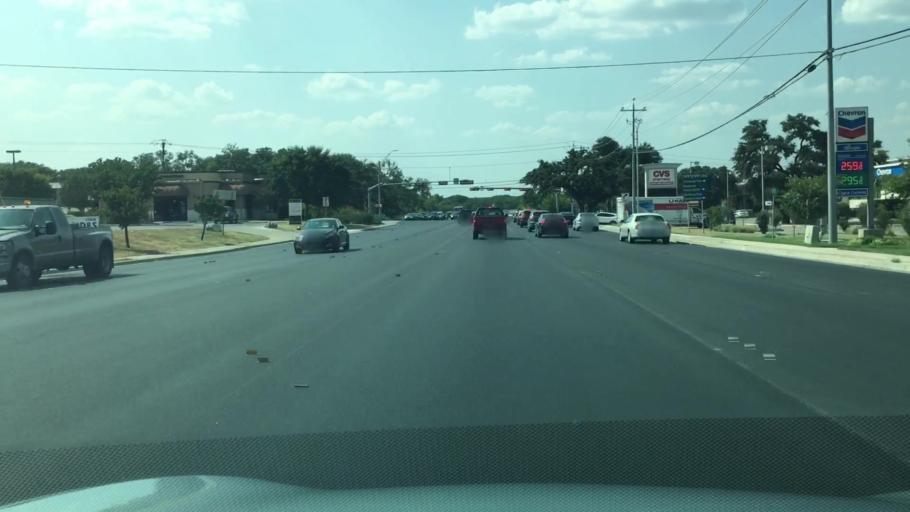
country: US
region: Texas
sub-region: Hays County
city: San Marcos
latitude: 29.8647
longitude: -97.9621
